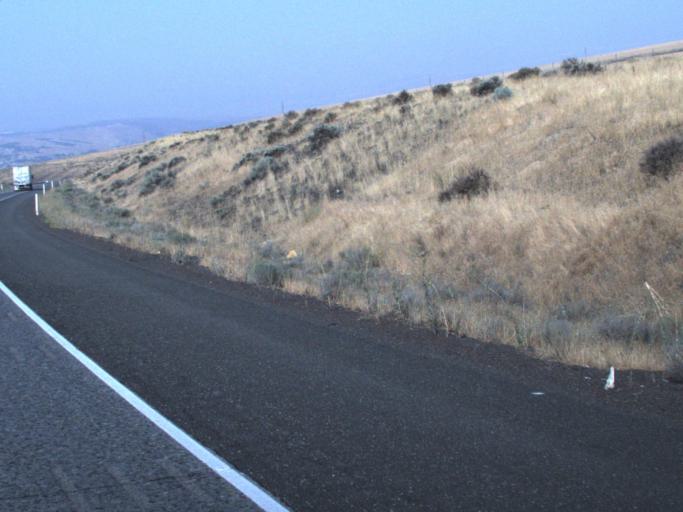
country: US
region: Washington
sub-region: Yakima County
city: Terrace Heights
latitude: 46.7137
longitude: -120.4158
